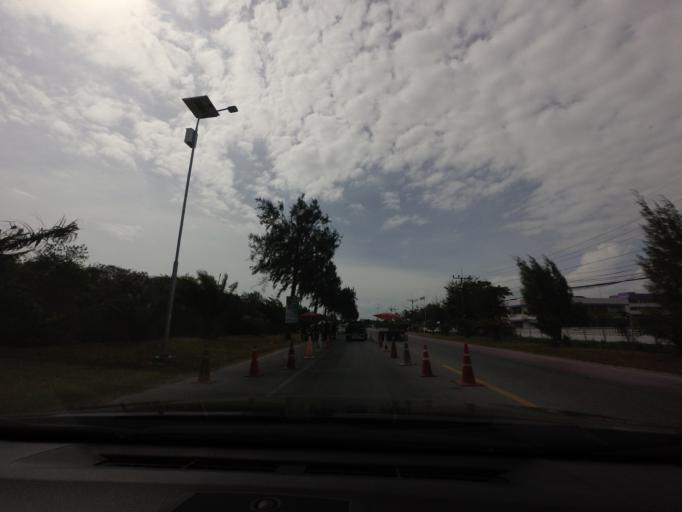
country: TH
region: Pattani
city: Pattani
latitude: 6.8838
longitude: 101.2447
